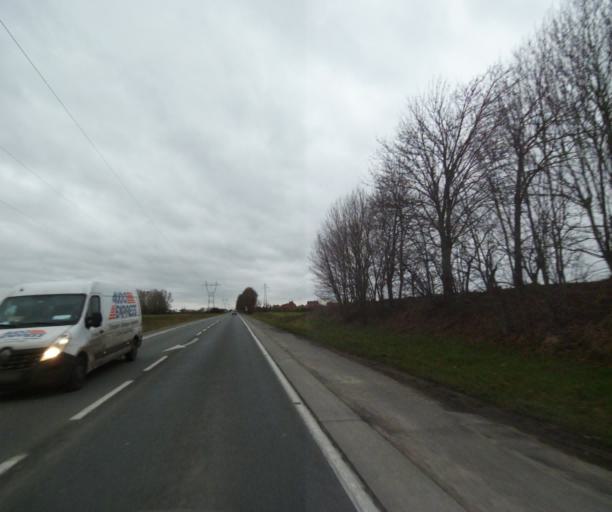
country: FR
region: Nord-Pas-de-Calais
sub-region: Departement du Nord
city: Marly
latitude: 50.3532
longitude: 3.5588
